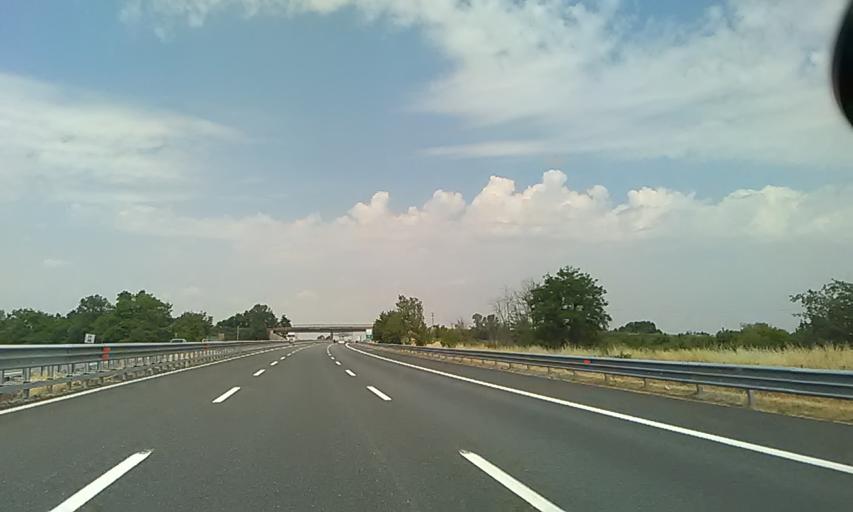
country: IT
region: Piedmont
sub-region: Provincia di Alessandria
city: Predosa
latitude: 44.7675
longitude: 8.6335
